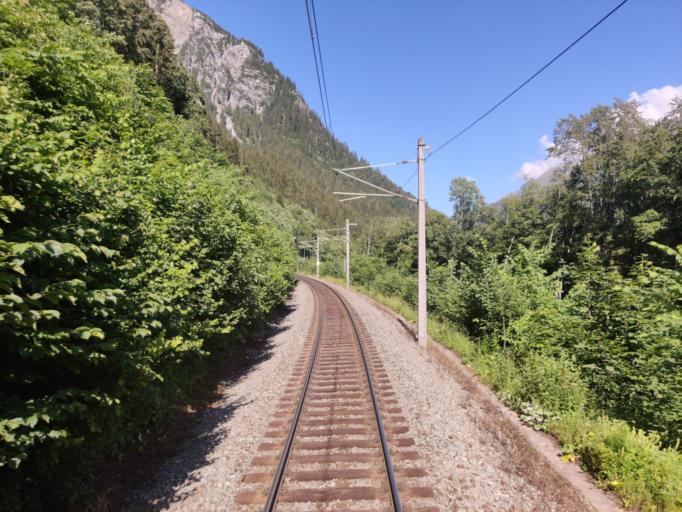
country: AT
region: Vorarlberg
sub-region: Politischer Bezirk Bludenz
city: Klosterle
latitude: 47.1338
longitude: 10.0851
